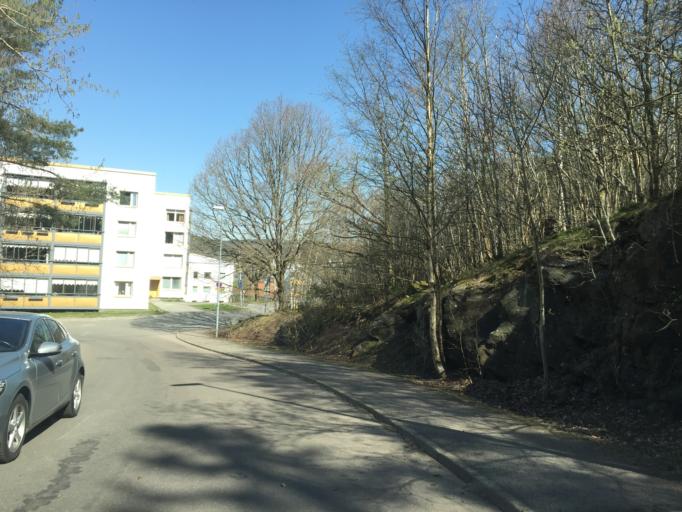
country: SE
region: Vaestra Goetaland
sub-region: Kungalvs Kommun
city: Kungalv
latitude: 57.8744
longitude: 11.9860
